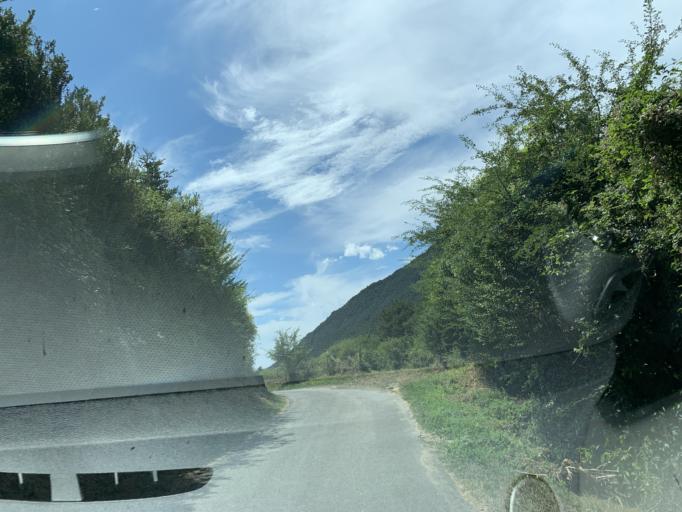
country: ES
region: Aragon
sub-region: Provincia de Huesca
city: Borau
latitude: 42.7168
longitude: -0.6018
